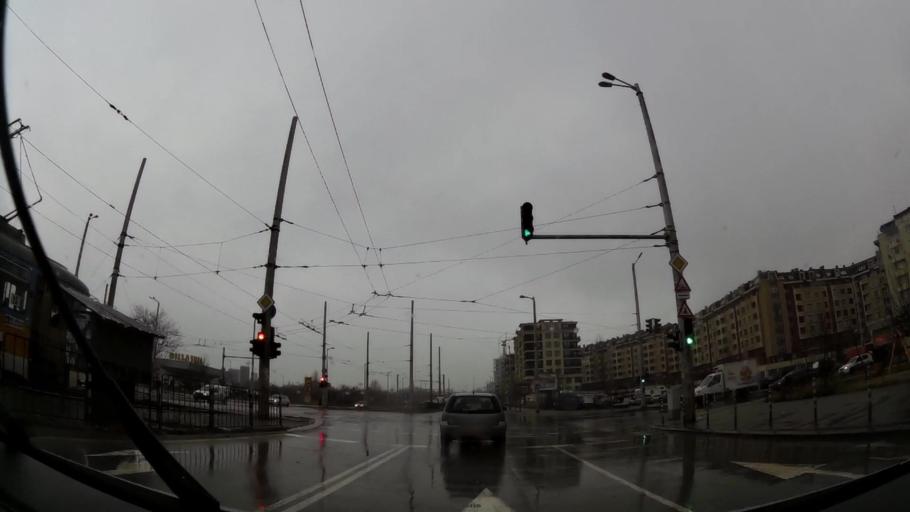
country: BG
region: Sofia-Capital
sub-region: Stolichna Obshtina
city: Sofia
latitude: 42.6479
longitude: 23.4036
